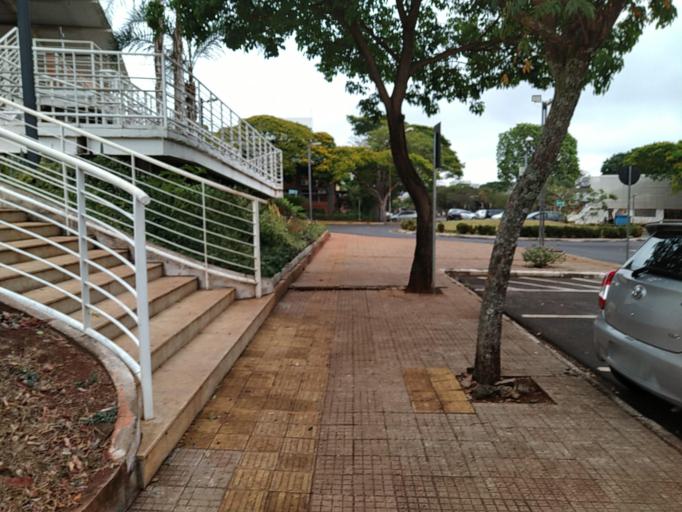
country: BR
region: Minas Gerais
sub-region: Uberlandia
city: Uberlandia
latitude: -18.9190
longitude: -48.2568
